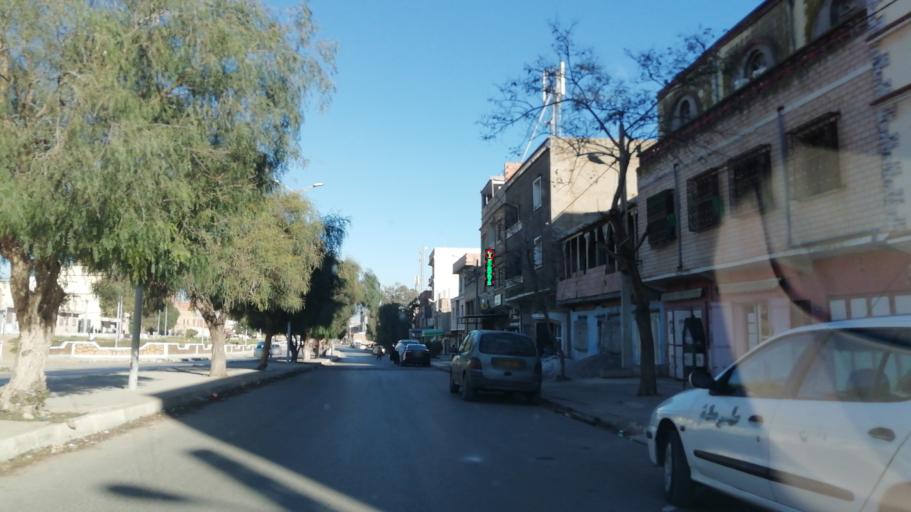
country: DZ
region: Oran
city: Bir el Djir
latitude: 35.7201
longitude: -0.5439
